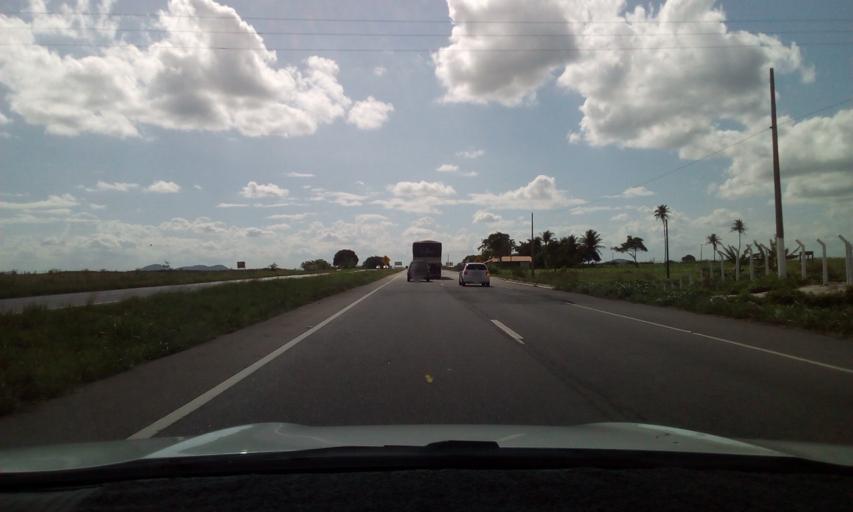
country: BR
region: Paraiba
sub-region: Pilar
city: Pilar
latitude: -7.1828
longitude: -35.3042
